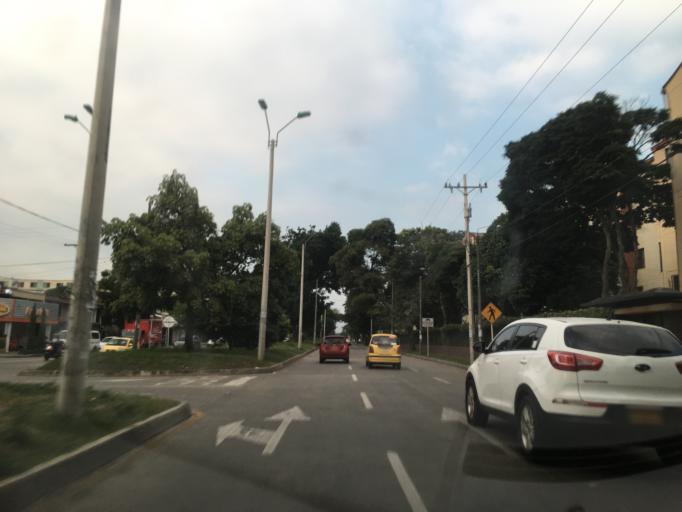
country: CO
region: Valle del Cauca
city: Cali
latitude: 3.4001
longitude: -76.5277
